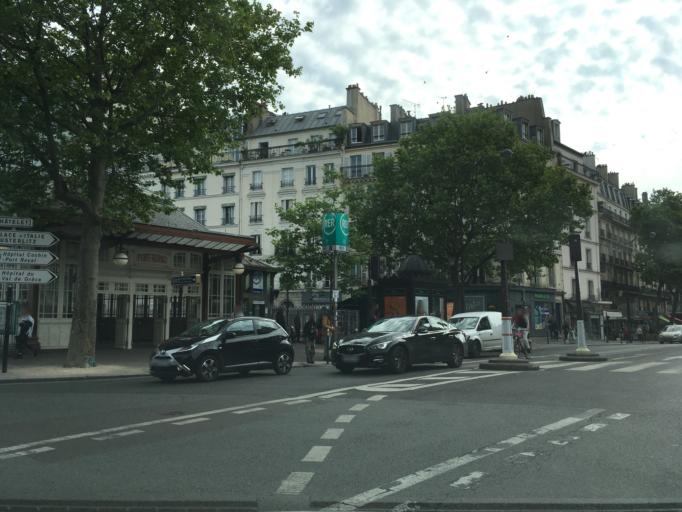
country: FR
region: Ile-de-France
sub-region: Paris
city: Paris
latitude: 48.8397
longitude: 2.3367
